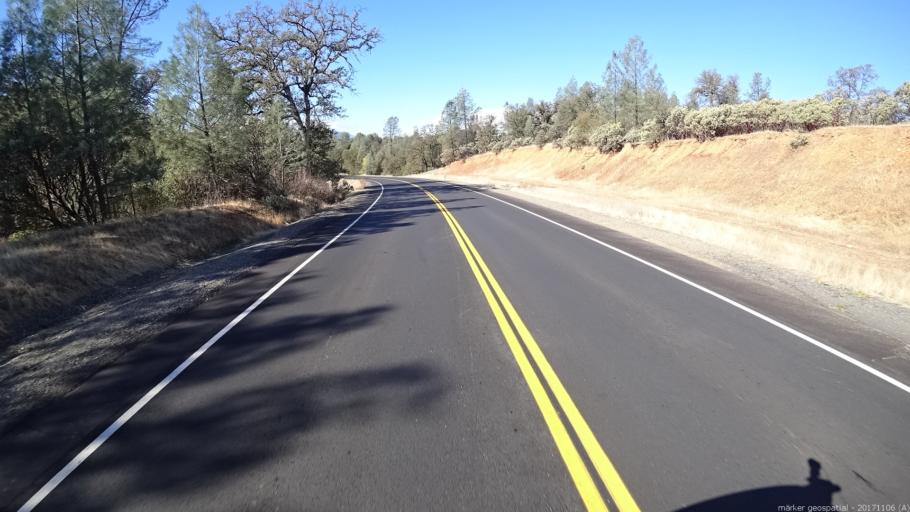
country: US
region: California
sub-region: Shasta County
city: Palo Cedro
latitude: 40.5930
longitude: -122.2921
